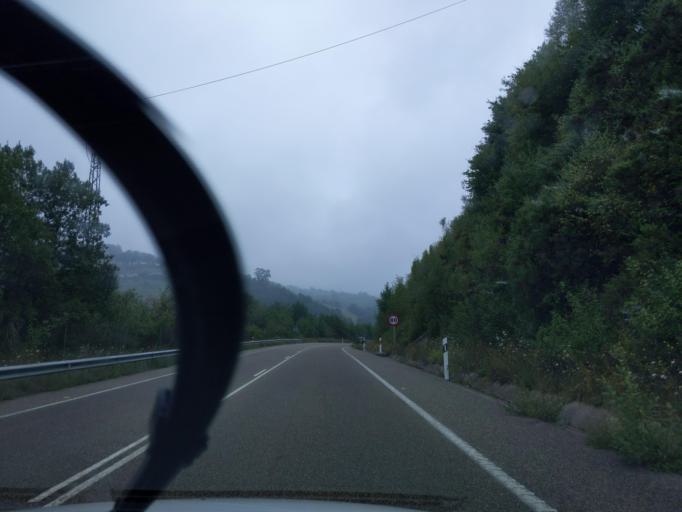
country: ES
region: Asturias
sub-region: Province of Asturias
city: El entrego
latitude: 43.3090
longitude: -5.6016
